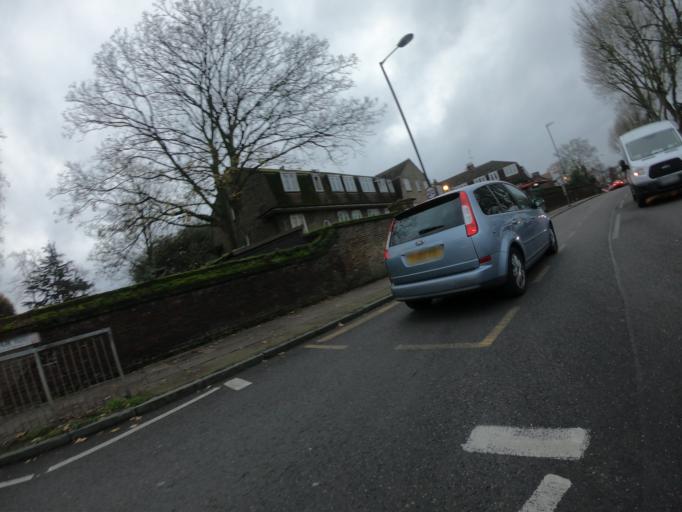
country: GB
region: England
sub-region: Greater London
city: Woolwich
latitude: 51.4820
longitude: 0.0405
